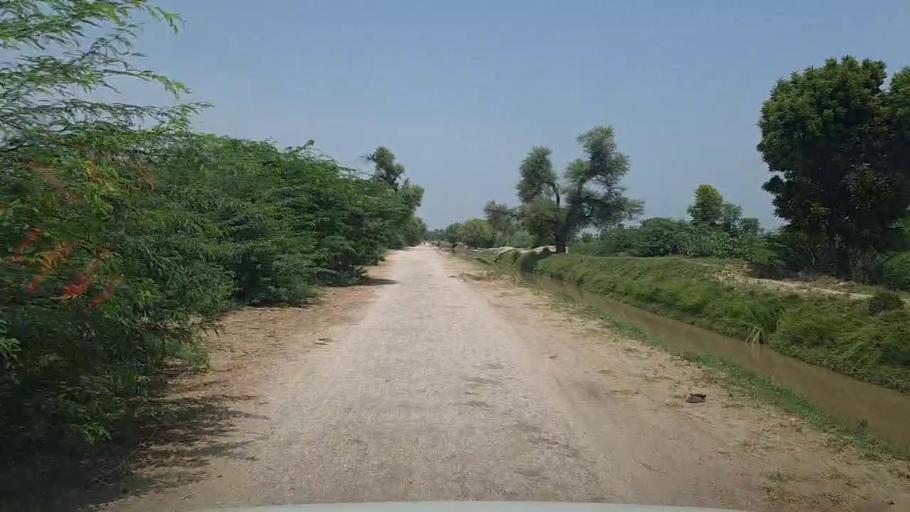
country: PK
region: Sindh
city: Karaundi
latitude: 26.8969
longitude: 68.3318
